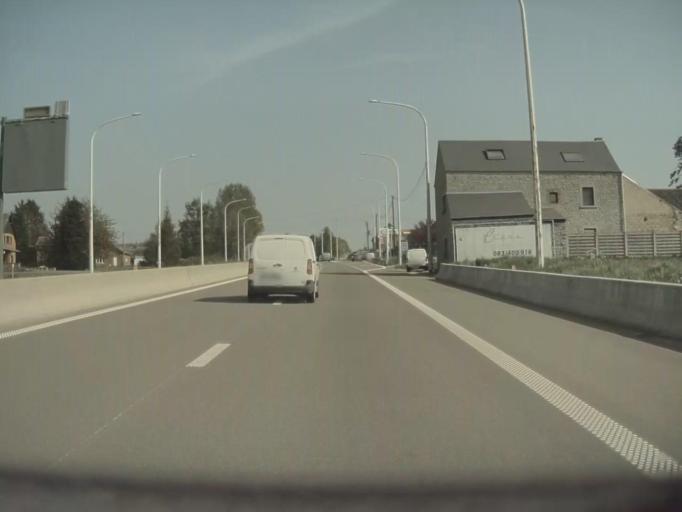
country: BE
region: Wallonia
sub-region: Province de Namur
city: Hamois
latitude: 50.3144
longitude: 5.1372
